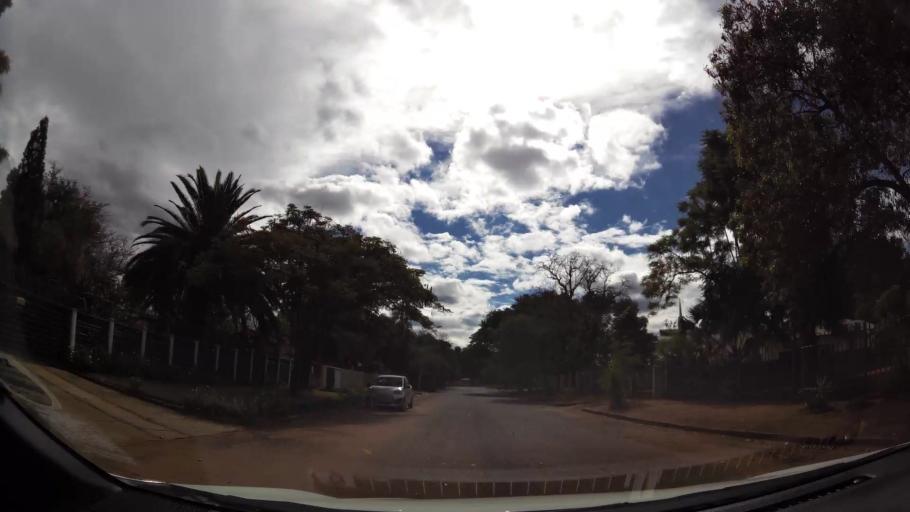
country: ZA
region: Limpopo
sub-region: Waterberg District Municipality
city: Warmbaths
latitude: -24.8871
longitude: 28.2796
